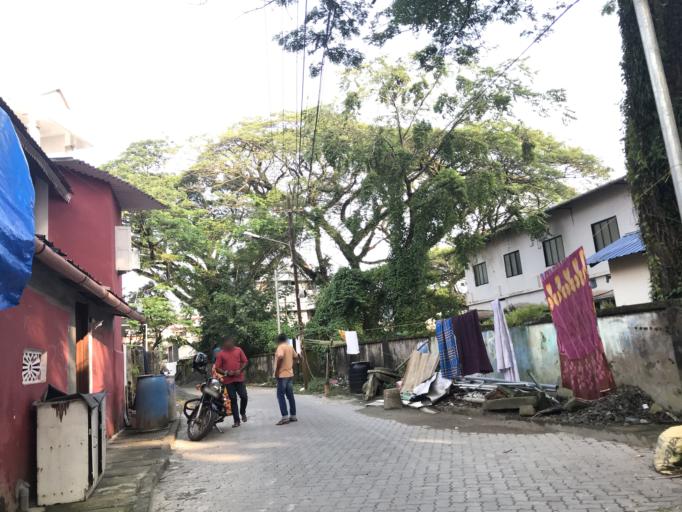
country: IN
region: Kerala
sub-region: Ernakulam
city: Cochin
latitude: 9.9664
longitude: 76.2466
